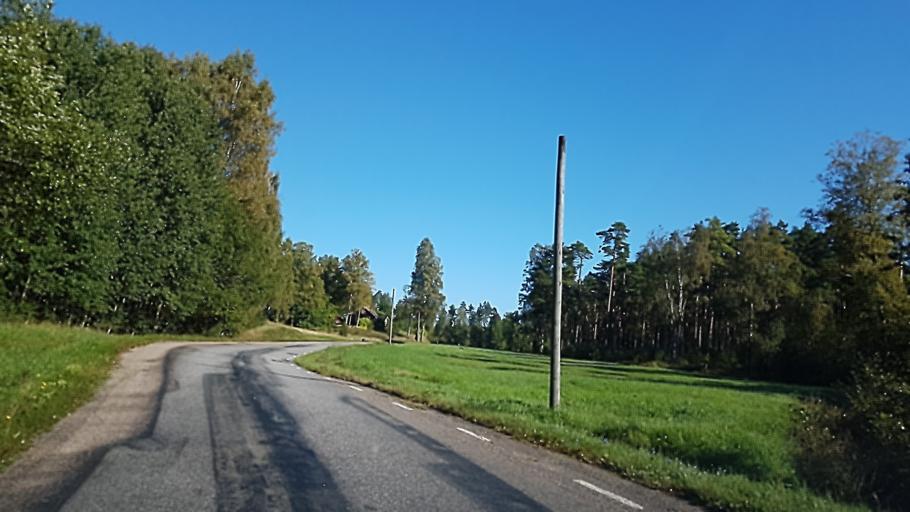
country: SE
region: Kronoberg
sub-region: Ljungby Kommun
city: Ljungby
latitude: 56.8128
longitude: 14.0355
